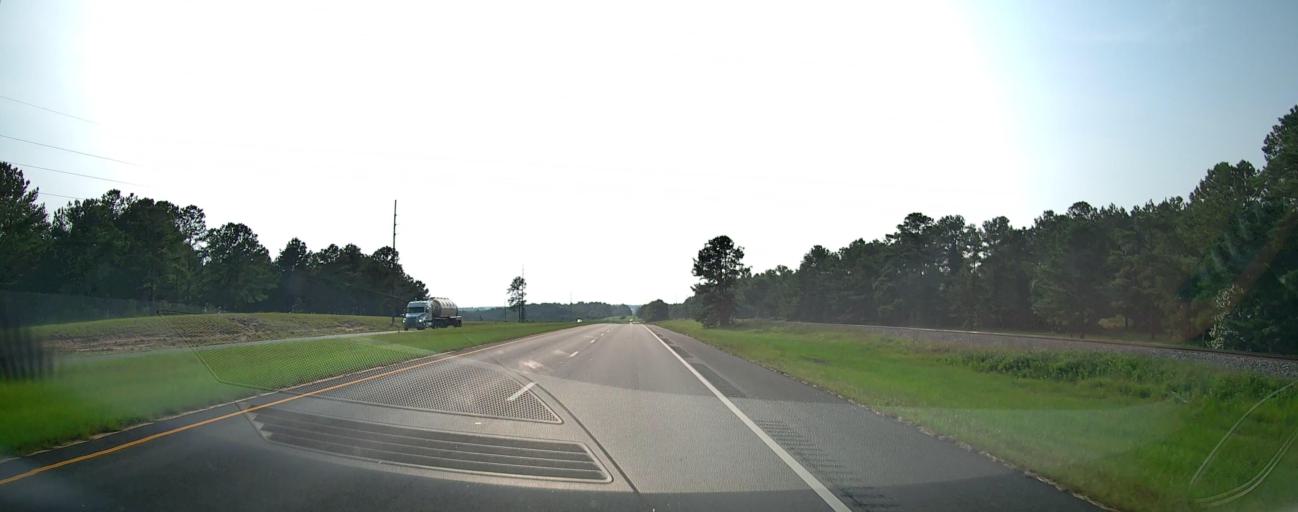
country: US
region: Georgia
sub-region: Taylor County
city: Butler
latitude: 32.5873
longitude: -84.3483
